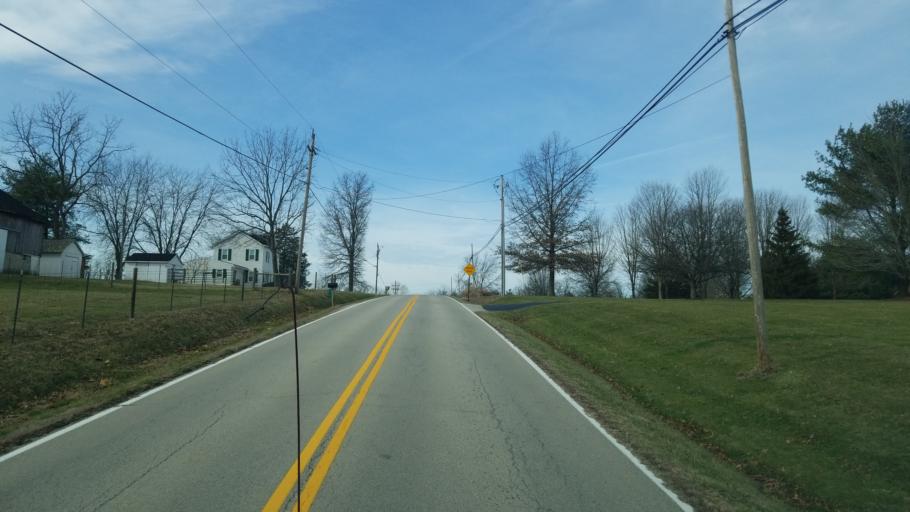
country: US
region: Ohio
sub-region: Warren County
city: Lebanon
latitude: 39.4288
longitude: -84.1395
